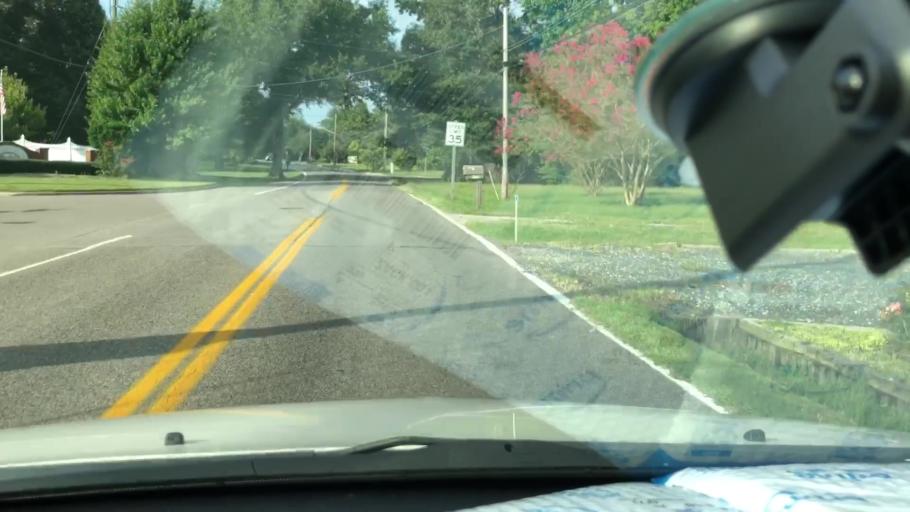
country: US
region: Virginia
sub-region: City of Chesapeake
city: Chesapeake
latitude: 36.7072
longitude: -76.2732
